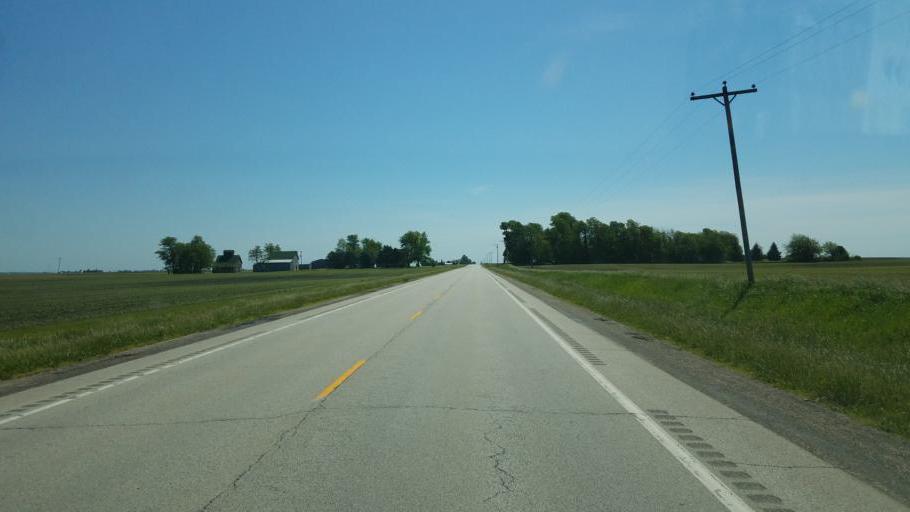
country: US
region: Illinois
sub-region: McLean County
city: Heyworth
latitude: 40.3123
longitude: -88.9178
